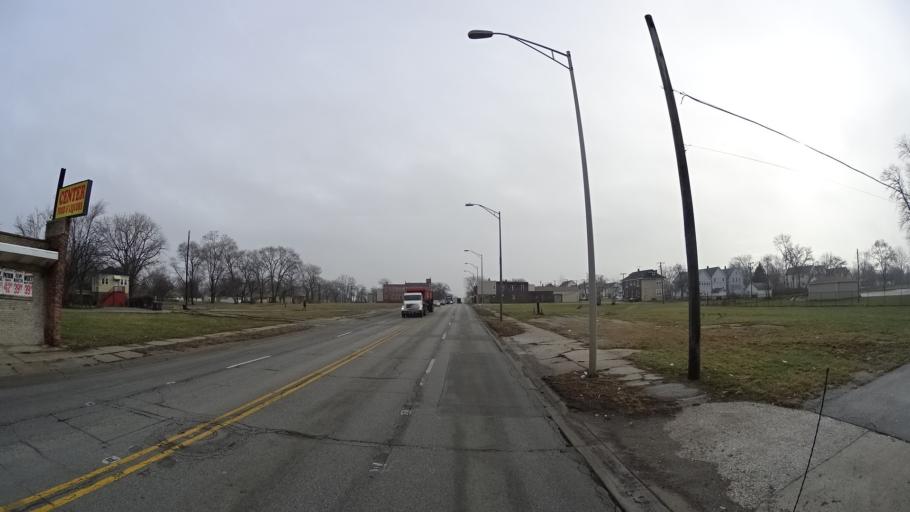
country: US
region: Illinois
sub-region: Cook County
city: Chicago Heights
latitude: 41.5063
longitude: -87.6273
